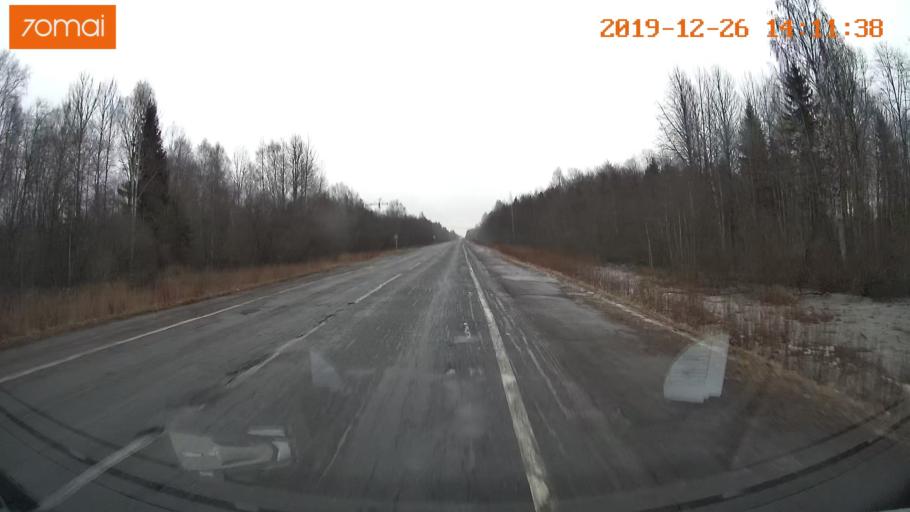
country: RU
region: Jaroslavl
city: Poshekhon'ye
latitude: 58.5099
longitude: 38.9760
